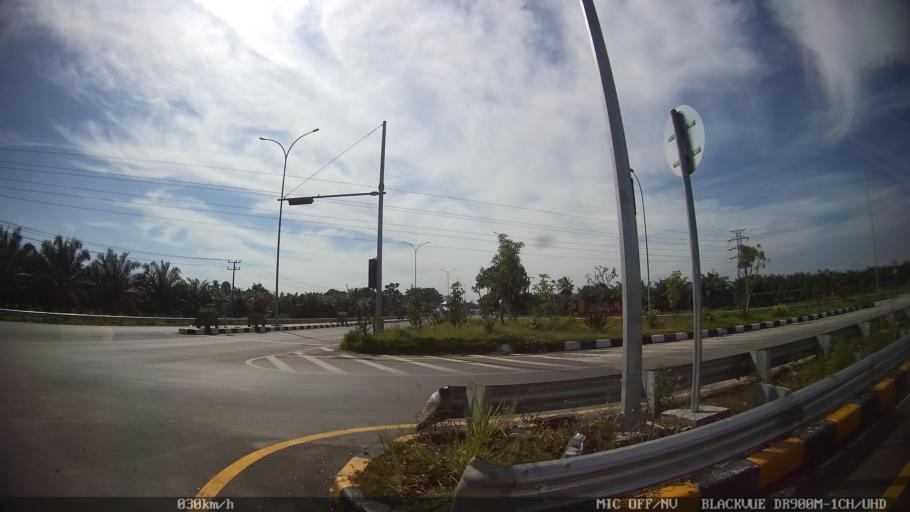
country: ID
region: North Sumatra
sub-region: Kabupaten Langkat
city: Stabat
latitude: 3.7322
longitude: 98.4908
